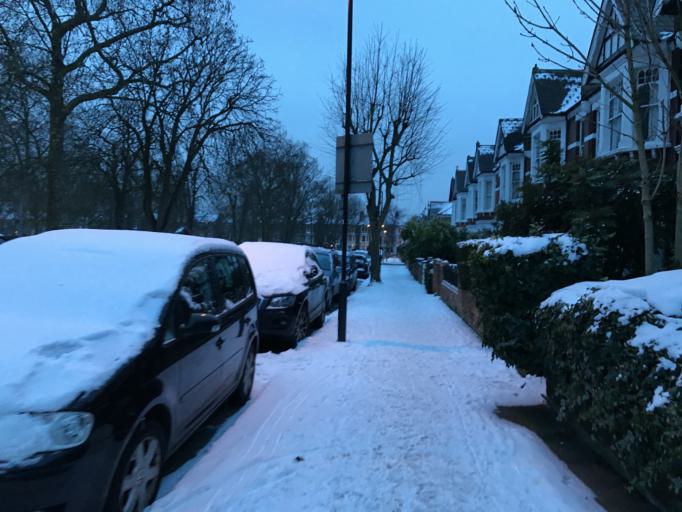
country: GB
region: England
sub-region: Greater London
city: Bayswater
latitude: 51.5348
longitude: -0.2124
